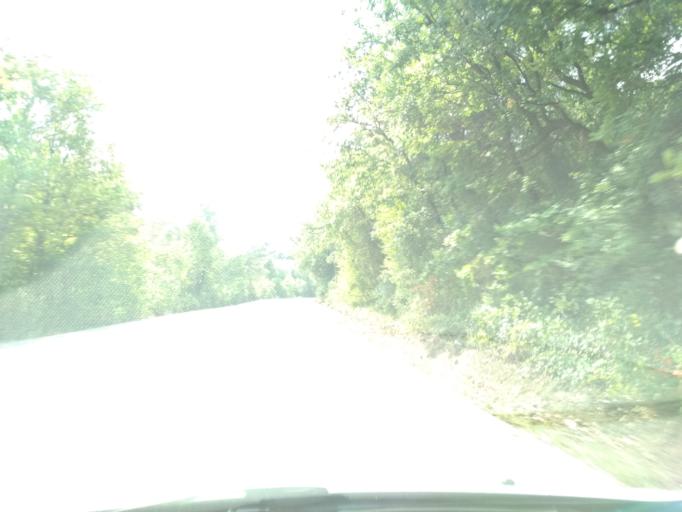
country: GR
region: Central Greece
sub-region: Nomos Evvoias
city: Prokopion
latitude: 38.7289
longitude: 23.5024
